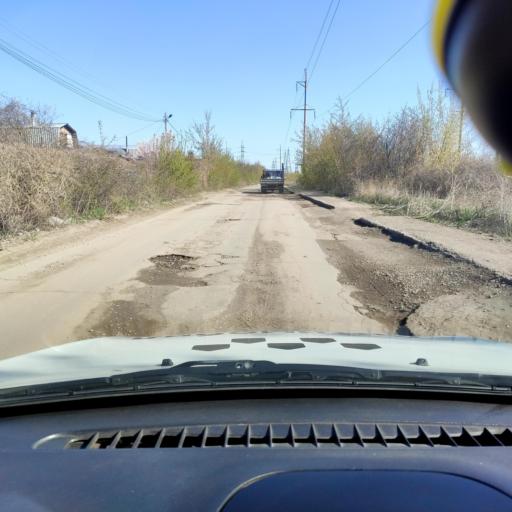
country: RU
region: Samara
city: Tol'yatti
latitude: 53.5835
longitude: 49.2941
